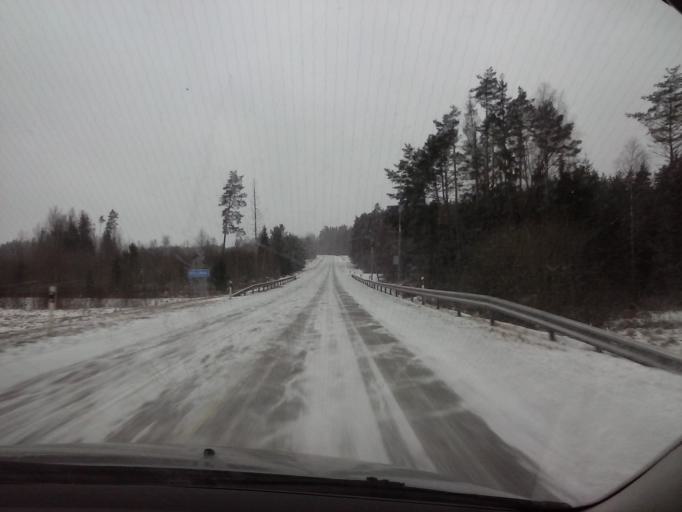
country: EE
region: Valgamaa
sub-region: Valga linn
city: Valga
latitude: 57.9804
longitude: 26.1723
